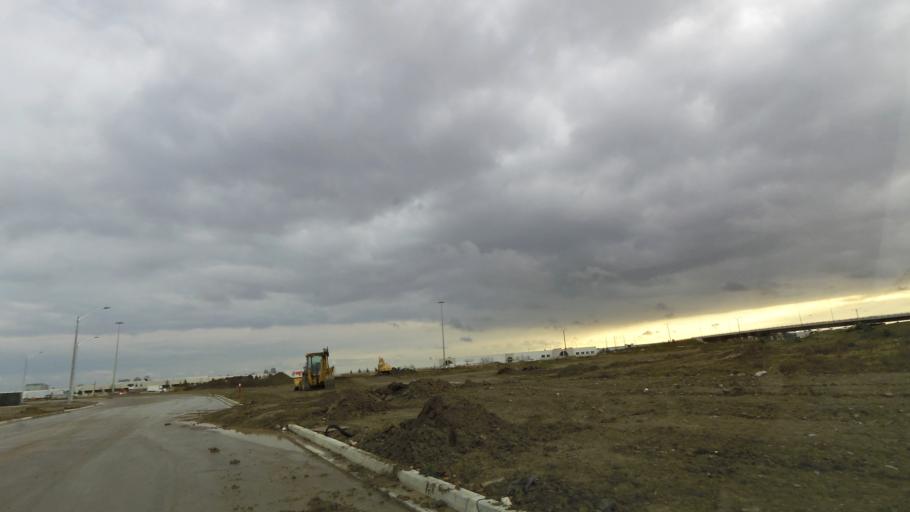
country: CA
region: Ontario
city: Mississauga
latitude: 43.6270
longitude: -79.6983
